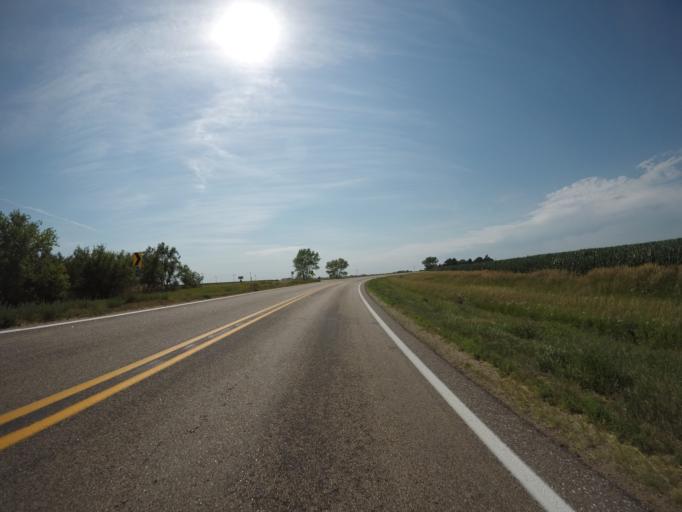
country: US
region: Nebraska
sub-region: Kearney County
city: Minden
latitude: 40.4809
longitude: -98.7959
